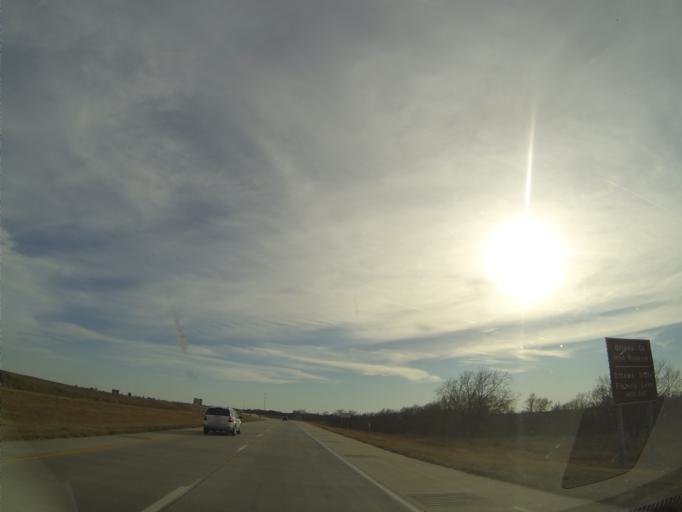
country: US
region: Kansas
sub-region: Ottawa County
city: Minneapolis
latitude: 39.1259
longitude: -97.6694
